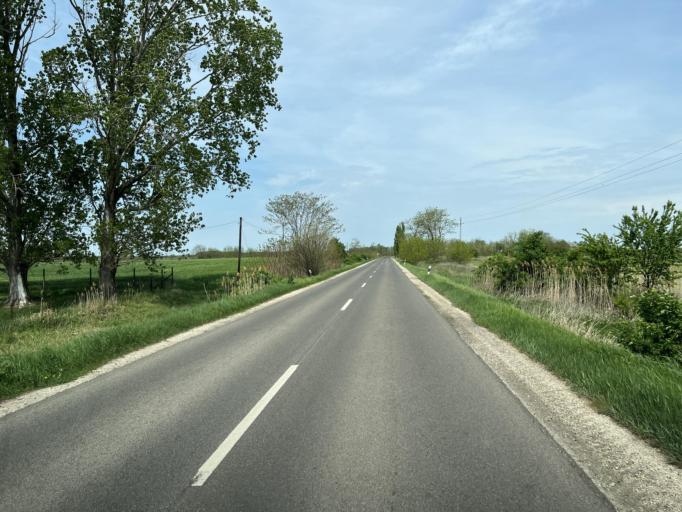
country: HU
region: Pest
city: Abony
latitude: 47.2190
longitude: 19.9768
